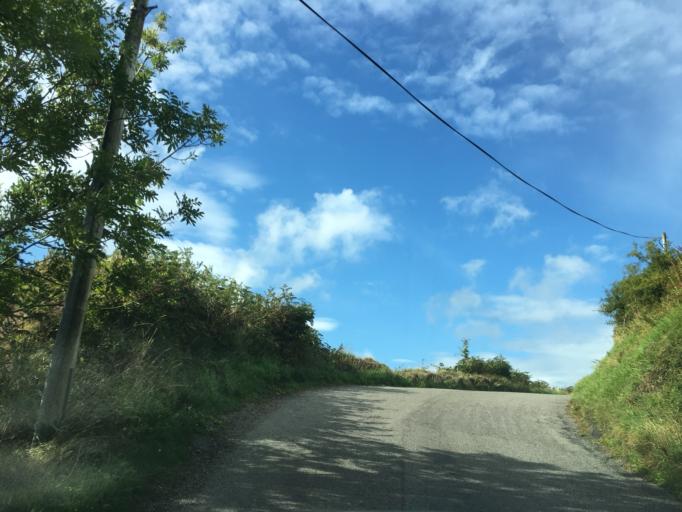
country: GB
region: Scotland
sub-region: Argyll and Bute
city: Oban
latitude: 56.2701
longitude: -5.6277
